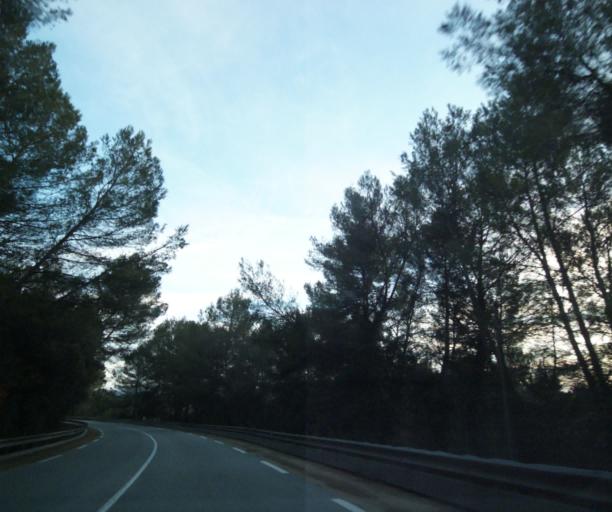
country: FR
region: Provence-Alpes-Cote d'Azur
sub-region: Departement du Var
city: La Motte
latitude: 43.4848
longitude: 6.5110
